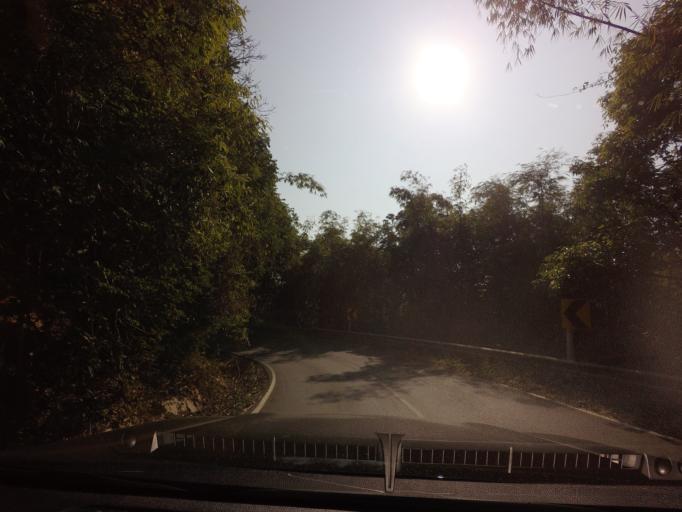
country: TH
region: Kanchanaburi
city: Thong Pha Phum
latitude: 14.6845
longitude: 98.4197
